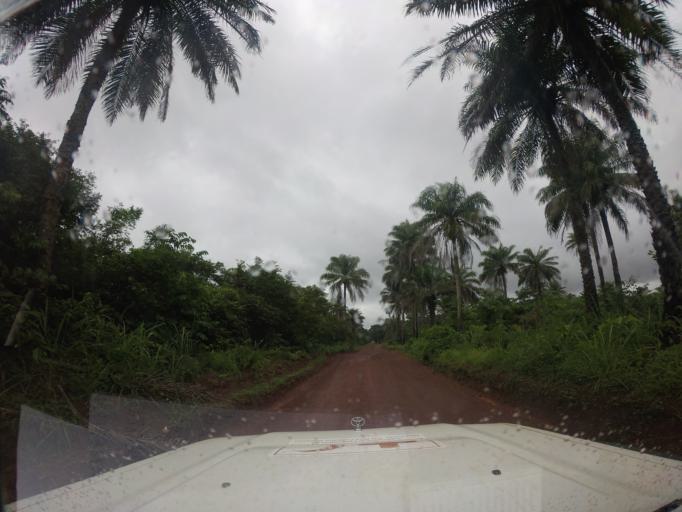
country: SL
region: Northern Province
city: Kambia
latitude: 9.1299
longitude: -12.8909
